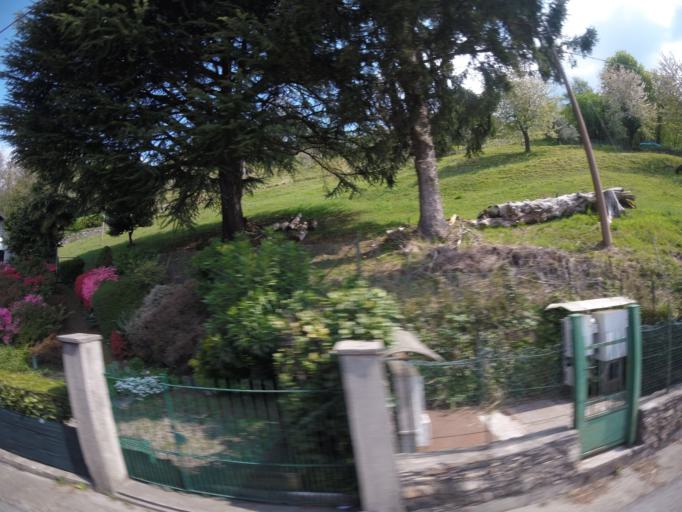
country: IT
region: Piedmont
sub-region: Provincia di Novara
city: Orta San Giulio
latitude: 45.8047
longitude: 8.4189
